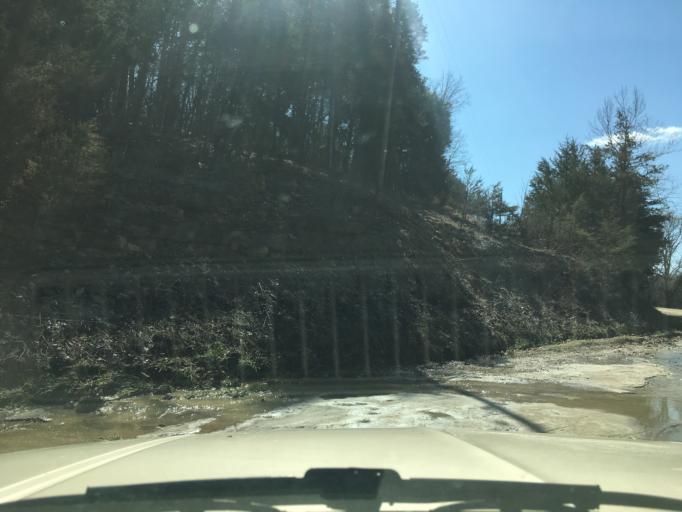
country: US
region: Missouri
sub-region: Franklin County
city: New Haven
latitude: 38.5535
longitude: -91.3247
